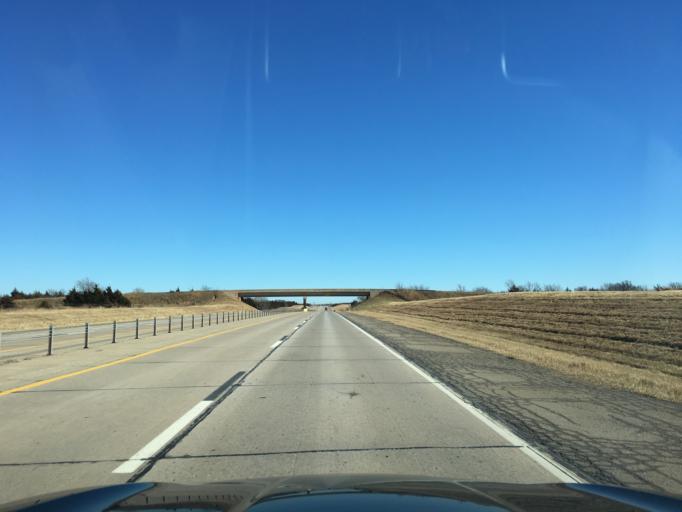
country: US
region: Oklahoma
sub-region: Pawnee County
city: Pawnee
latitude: 36.2249
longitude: -96.8394
